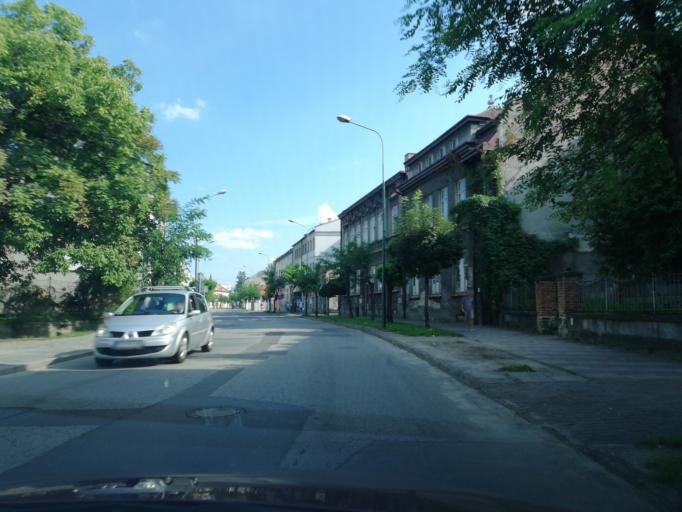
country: PL
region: Lesser Poland Voivodeship
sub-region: Powiat nowosadecki
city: Nowy Sacz
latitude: 49.6184
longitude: 20.6974
